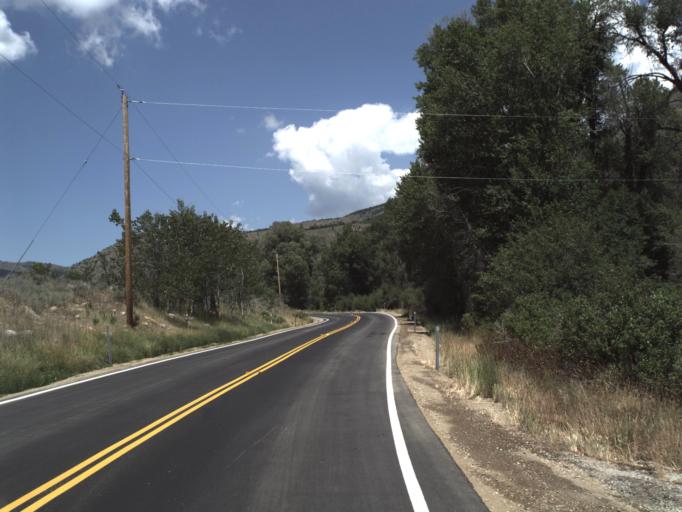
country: US
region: Utah
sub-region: Weber County
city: Wolf Creek
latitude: 41.3012
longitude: -111.6185
